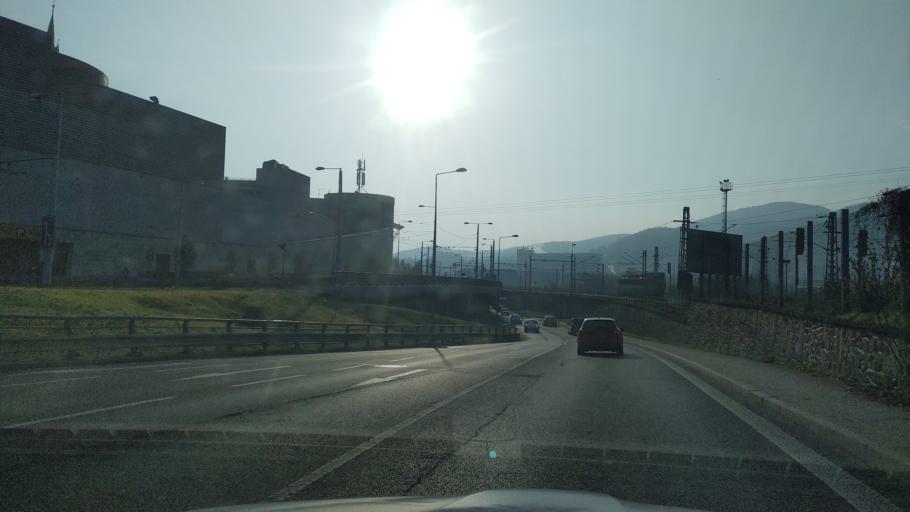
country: CZ
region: Ustecky
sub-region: Okres Usti nad Labem
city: Usti nad Labem
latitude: 50.6583
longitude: 14.0377
